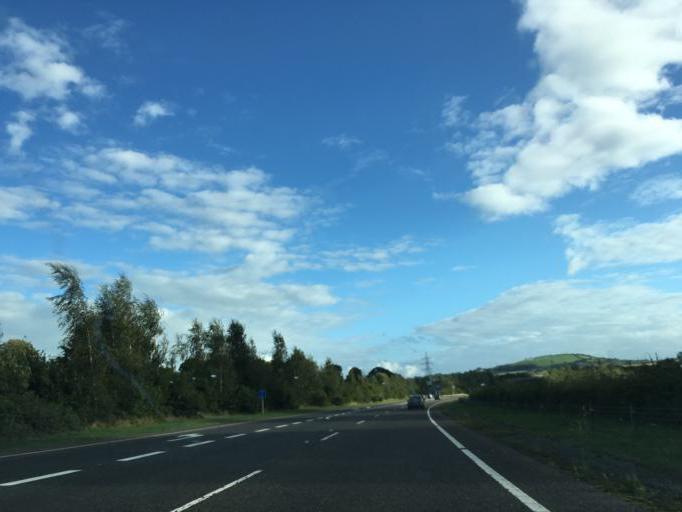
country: IE
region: Leinster
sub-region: Wicklow
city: Rathnew
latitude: 53.0054
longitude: -6.0918
